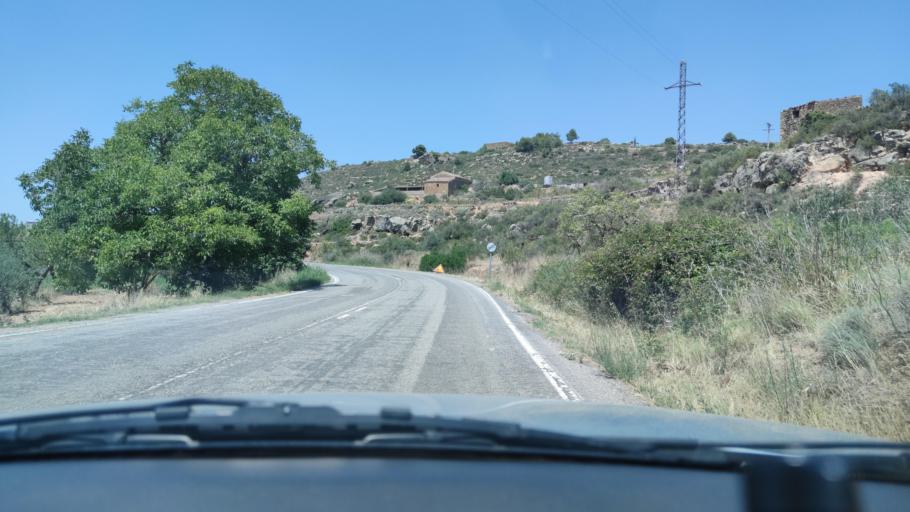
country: ES
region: Catalonia
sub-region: Provincia de Lleida
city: el Cogul
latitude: 41.4134
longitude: 0.6872
